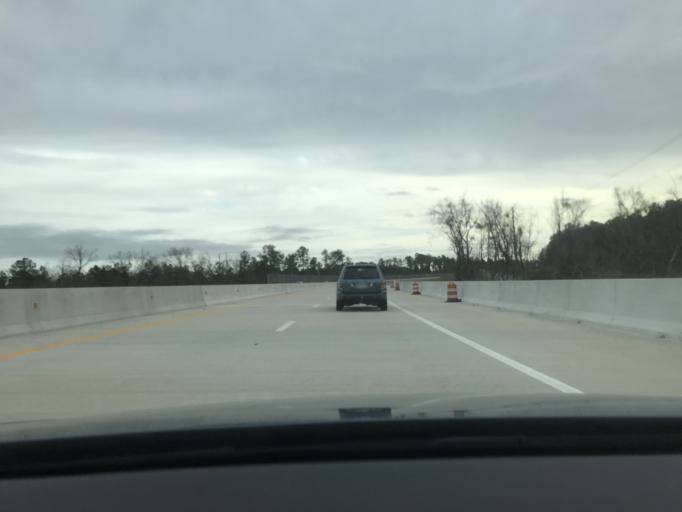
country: US
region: North Carolina
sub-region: Cumberland County
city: Fort Bragg
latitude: 35.0804
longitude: -79.0213
